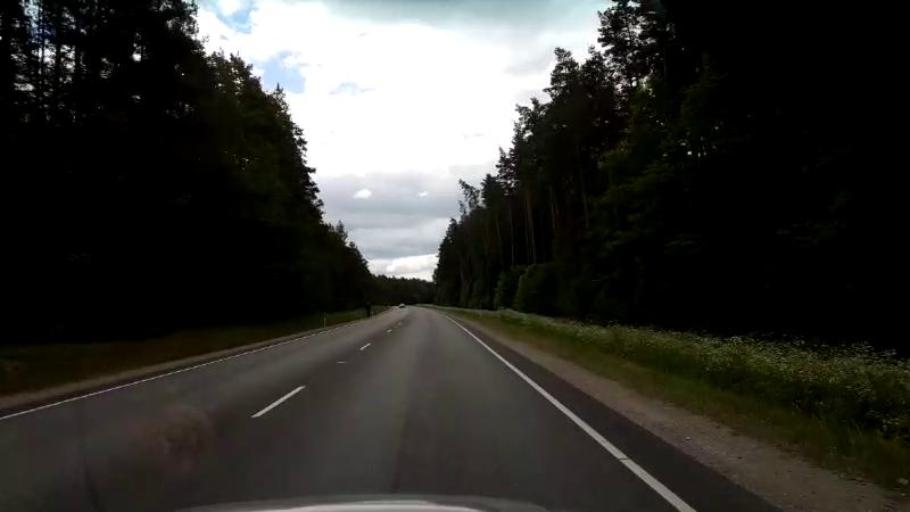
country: EE
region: Paernumaa
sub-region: Paikuse vald
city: Paikuse
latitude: 58.3312
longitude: 24.5955
